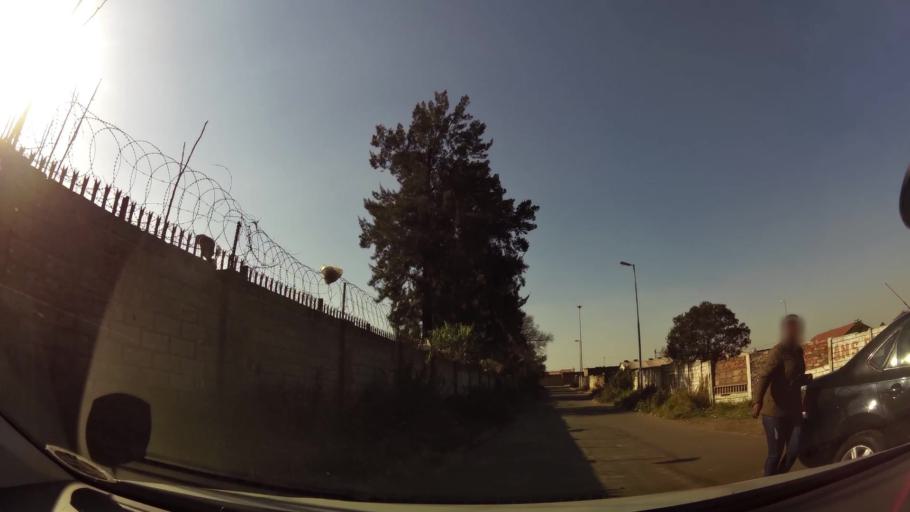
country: ZA
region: Gauteng
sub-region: City of Johannesburg Metropolitan Municipality
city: Soweto
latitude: -26.2790
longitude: 27.8743
